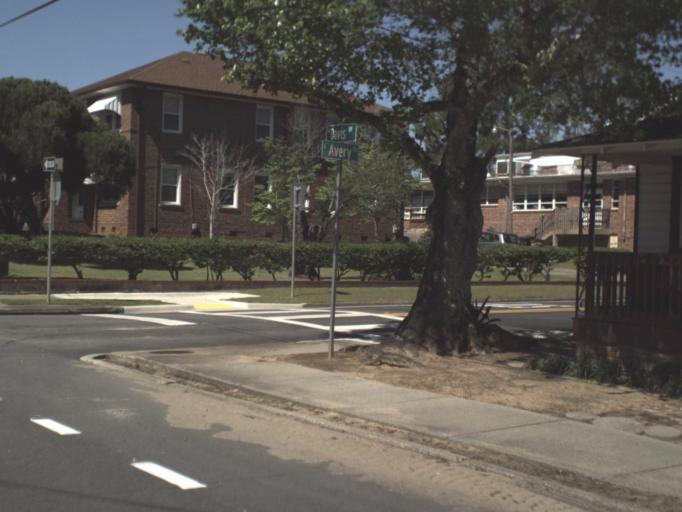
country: US
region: Florida
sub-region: Escambia County
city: Pensacola
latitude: 30.4318
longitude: -87.2127
